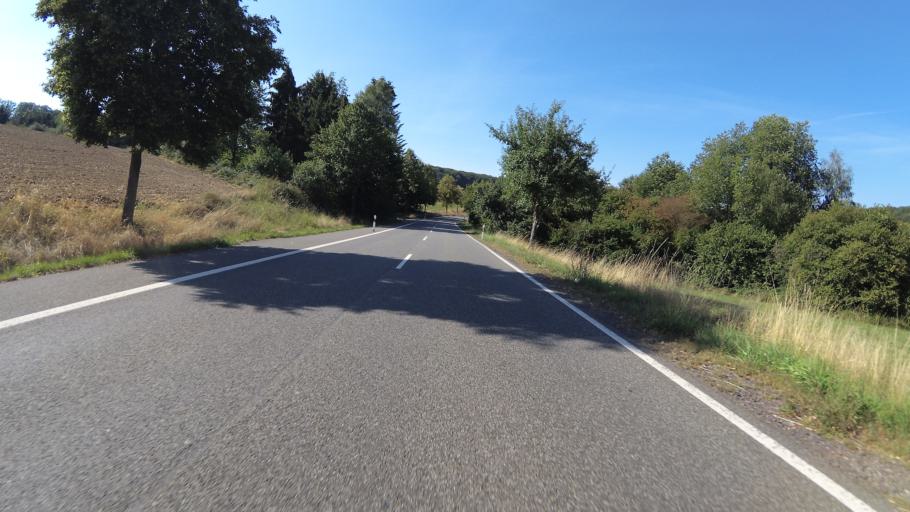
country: DE
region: Saarland
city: Eppelborn
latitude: 49.3811
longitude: 6.9641
